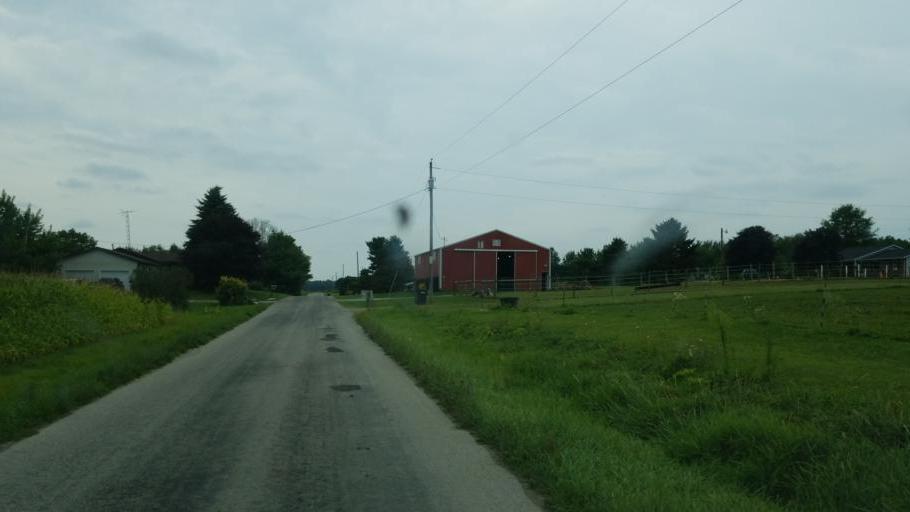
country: US
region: Ohio
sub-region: Morrow County
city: Mount Gilead
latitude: 40.5197
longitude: -82.8045
